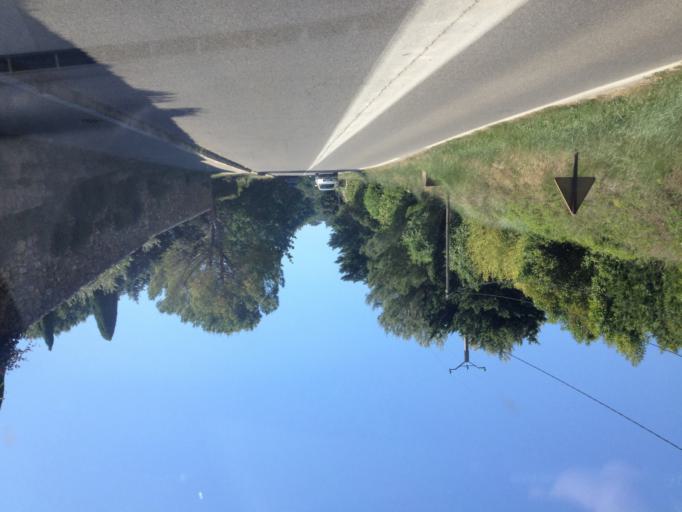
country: FR
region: Provence-Alpes-Cote d'Azur
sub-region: Departement du Vaucluse
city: Lourmarin
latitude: 43.7611
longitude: 5.3647
